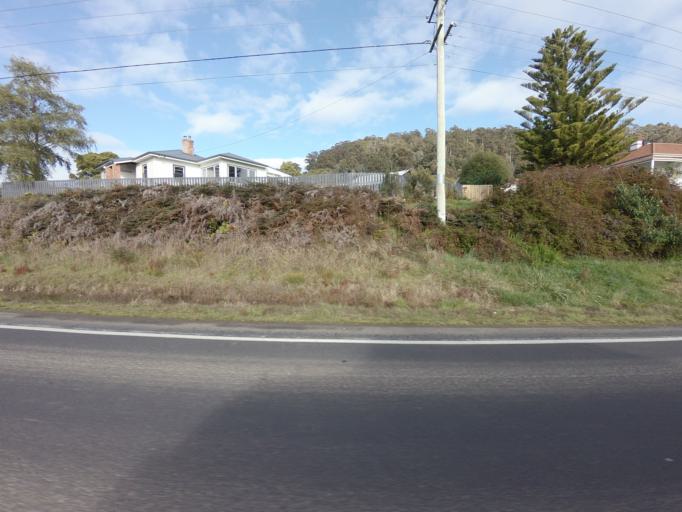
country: AU
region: Tasmania
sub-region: Huon Valley
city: Franklin
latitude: -43.0775
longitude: 147.0173
